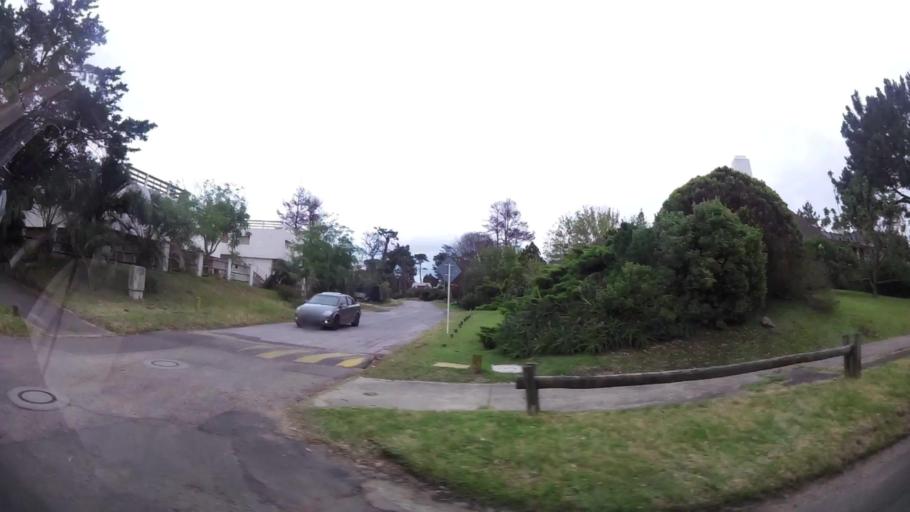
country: UY
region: Maldonado
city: Maldonado
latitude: -34.9069
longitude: -54.9985
